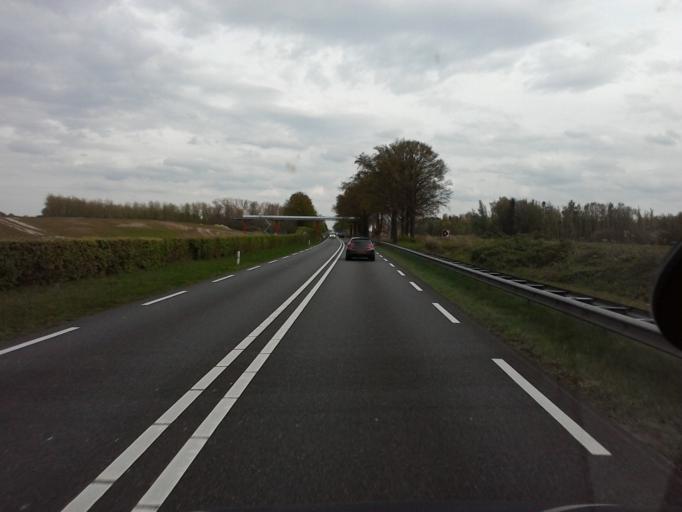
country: NL
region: North Brabant
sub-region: Gemeente Veghel
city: Eerde
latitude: 51.6336
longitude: 5.4855
